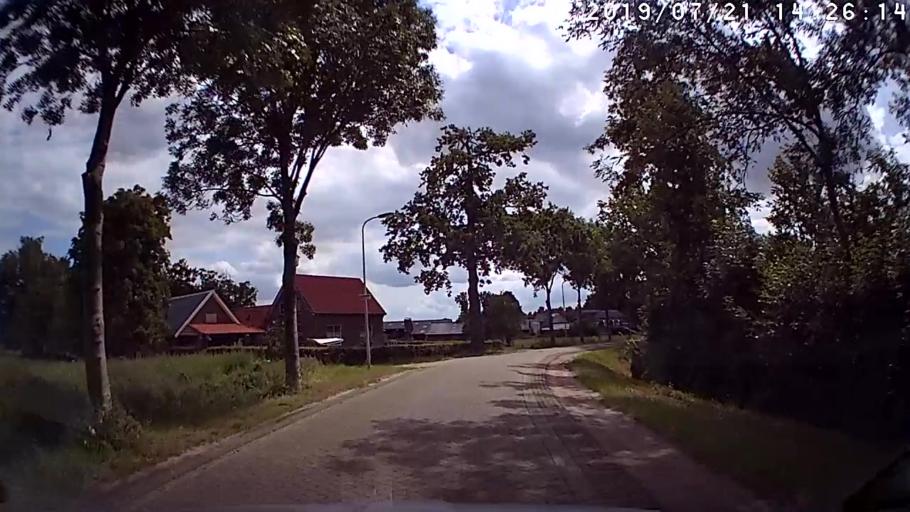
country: NL
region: Overijssel
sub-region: Gemeente Raalte
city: Heino
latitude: 52.4389
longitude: 6.1920
